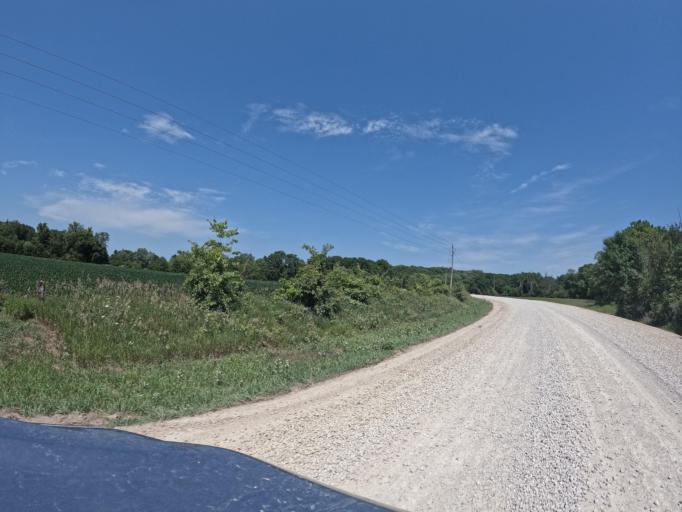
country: US
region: Iowa
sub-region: Henry County
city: Mount Pleasant
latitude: 40.9048
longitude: -91.6730
